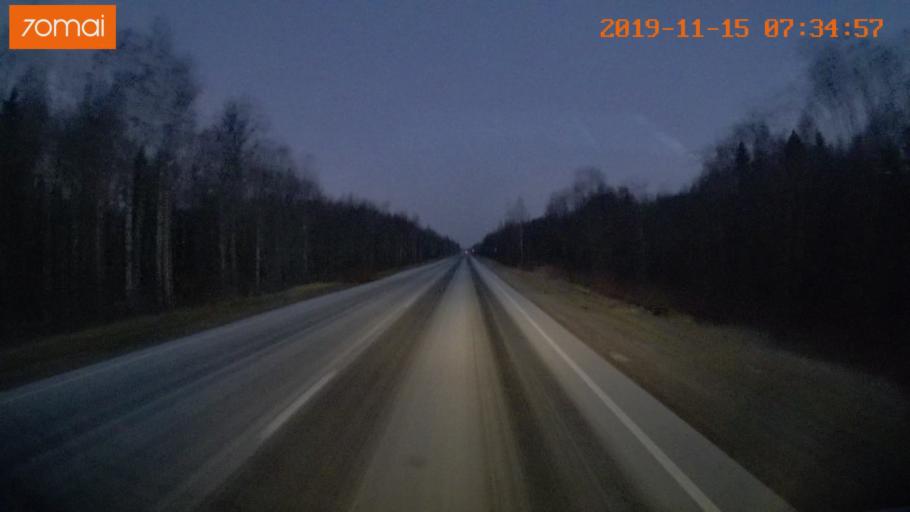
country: RU
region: Vologda
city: Sheksna
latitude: 58.7244
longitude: 38.4615
